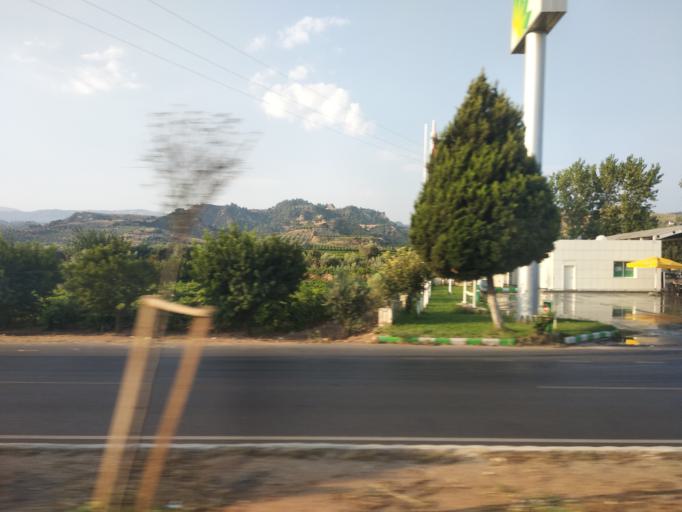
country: TR
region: Manisa
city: Ahmetli
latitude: 38.5072
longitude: 27.9918
